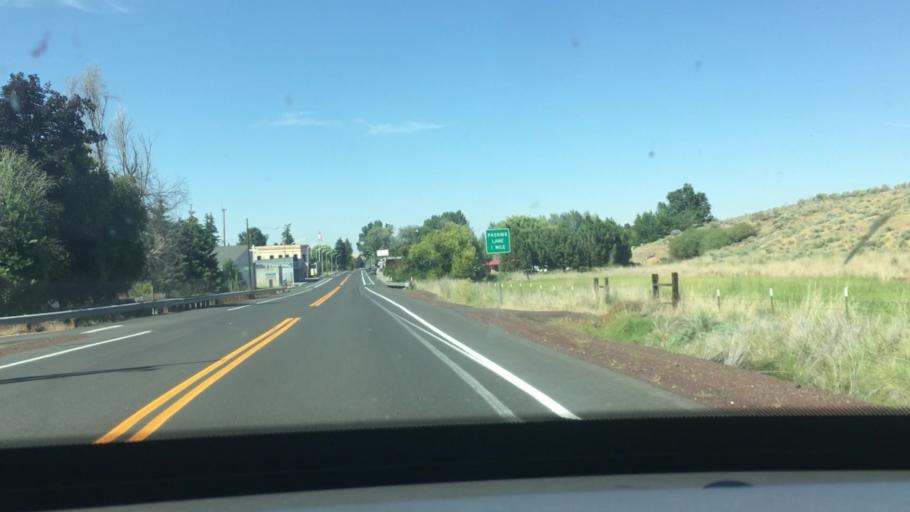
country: US
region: Oregon
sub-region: Sherman County
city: Moro
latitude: 45.3580
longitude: -120.7857
